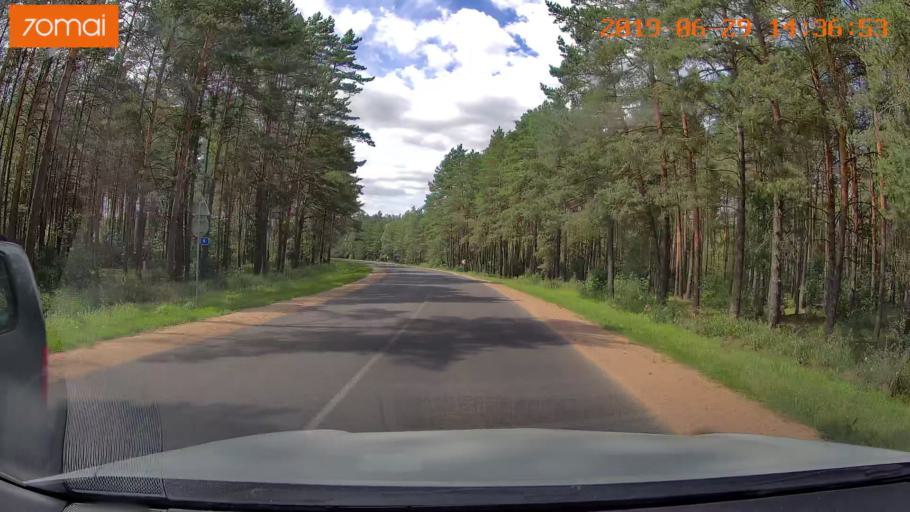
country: BY
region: Minsk
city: Starobin
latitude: 52.7493
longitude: 27.4749
